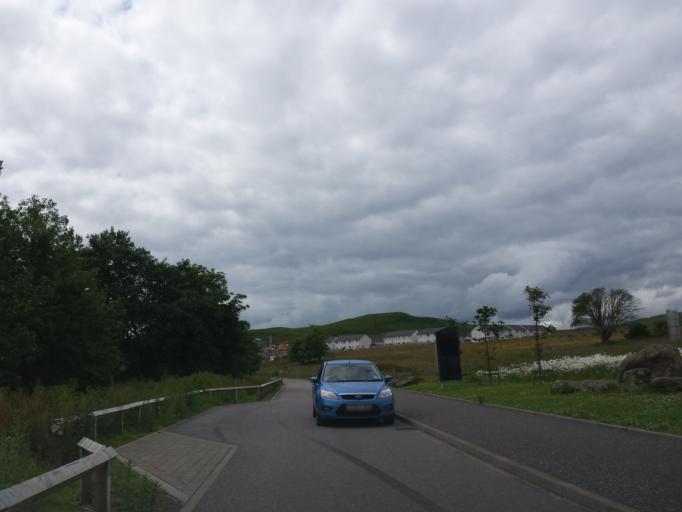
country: GB
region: Scotland
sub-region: Argyll and Bute
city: Oban
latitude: 56.4504
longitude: -5.4430
